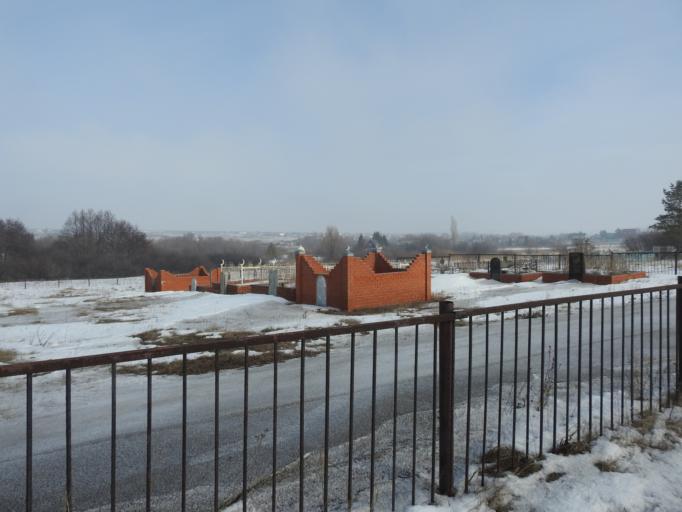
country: RU
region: Saratov
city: Krasnyy Oktyabr'
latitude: 51.4950
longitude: 45.7671
